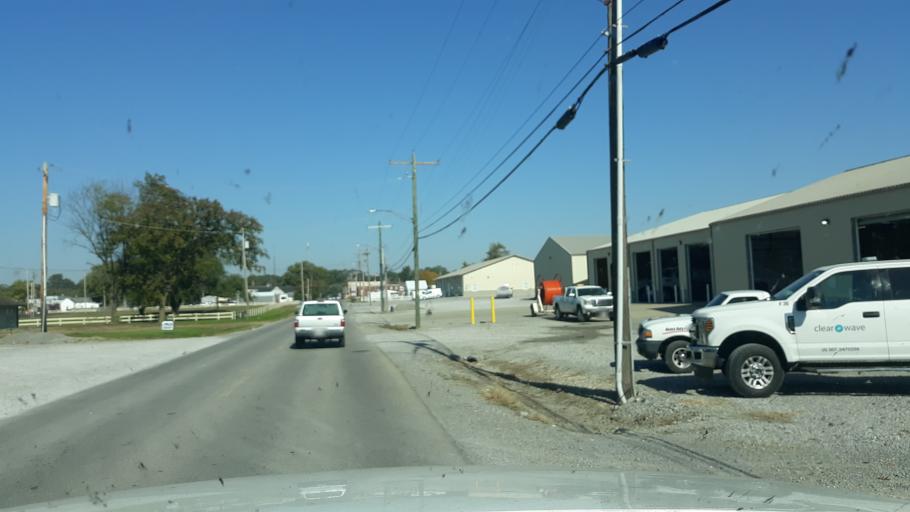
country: US
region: Illinois
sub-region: Saline County
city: Eldorado
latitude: 37.8097
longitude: -88.4352
